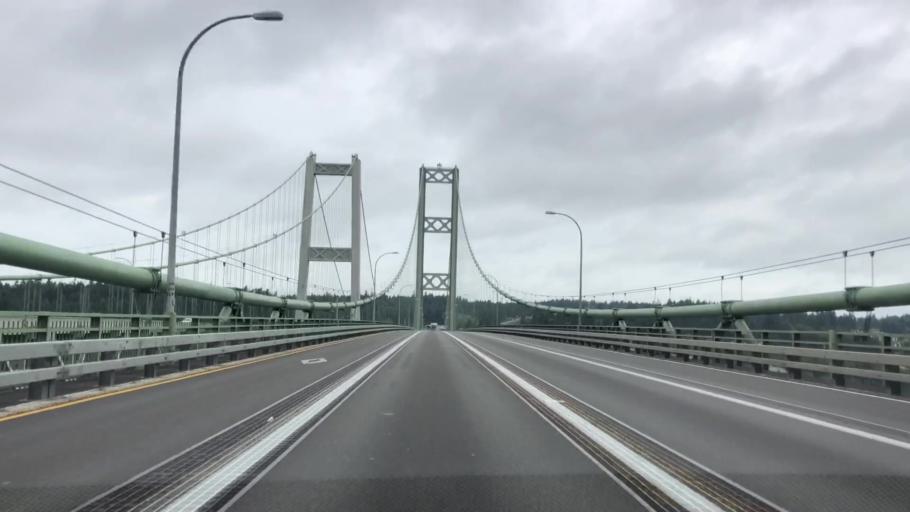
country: US
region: Washington
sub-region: Pierce County
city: University Place
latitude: 47.2682
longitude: -122.5502
